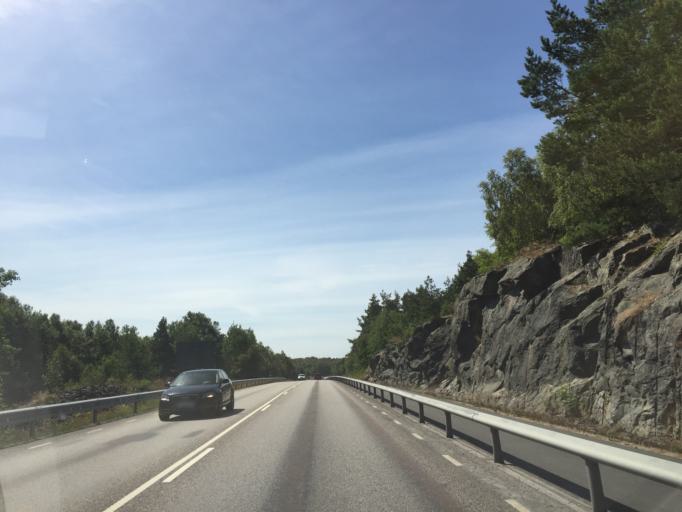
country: SE
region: Vaestra Goetaland
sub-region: Lysekils Kommun
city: Lysekil
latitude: 58.3012
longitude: 11.4750
